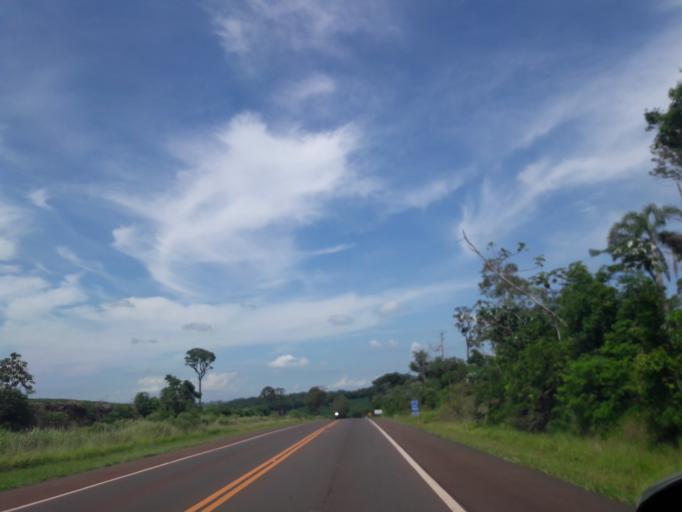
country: BR
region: Parana
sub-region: Campo Mourao
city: Campo Mourao
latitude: -24.2850
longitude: -52.5536
